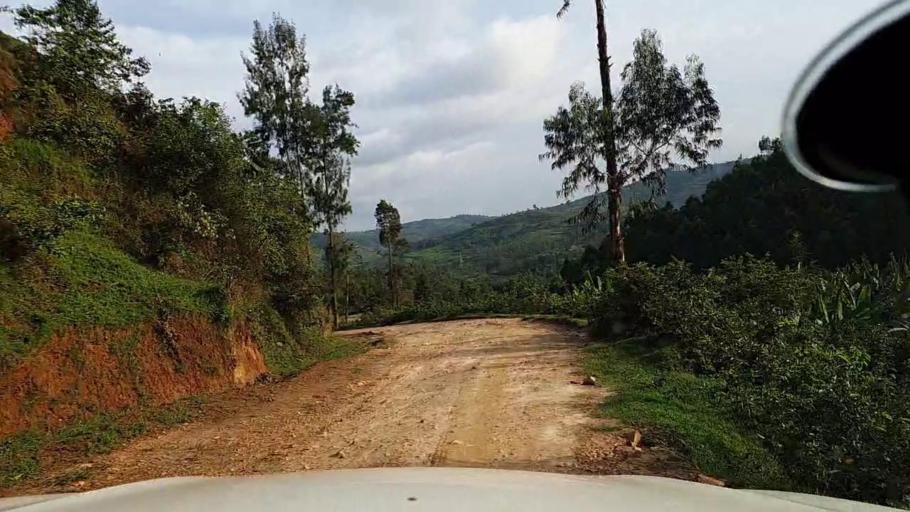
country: RW
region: Southern Province
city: Gitarama
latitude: -2.1907
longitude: 29.5781
